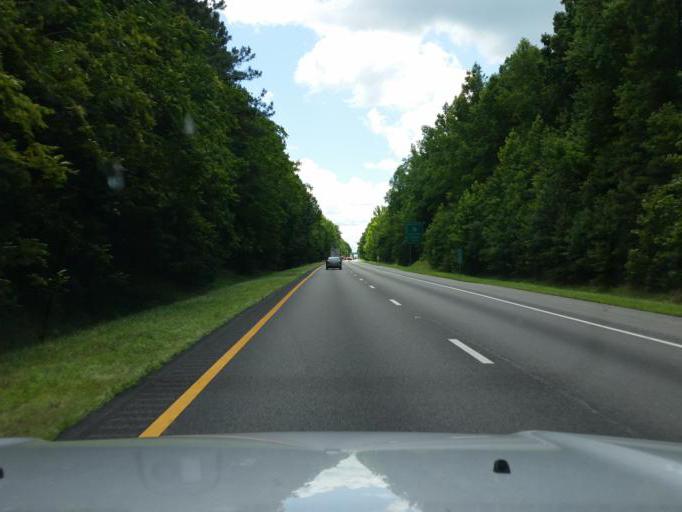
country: US
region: Virginia
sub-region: James City County
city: Williamsburg
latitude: 37.4000
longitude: -76.7796
